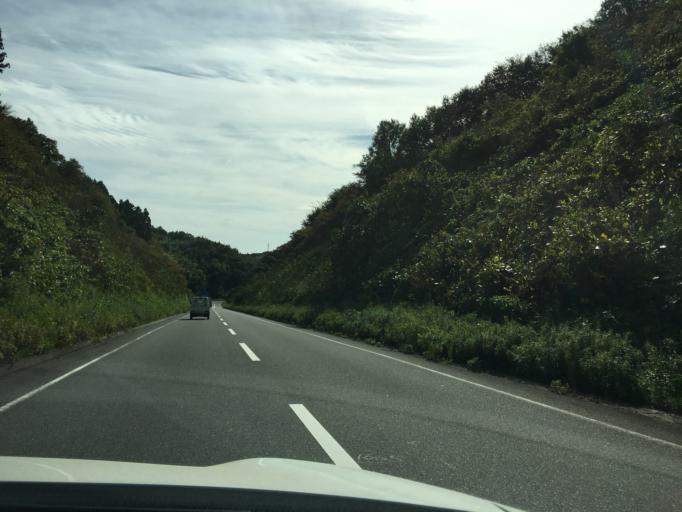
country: JP
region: Fukushima
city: Nihommatsu
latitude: 37.5513
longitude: 140.4996
